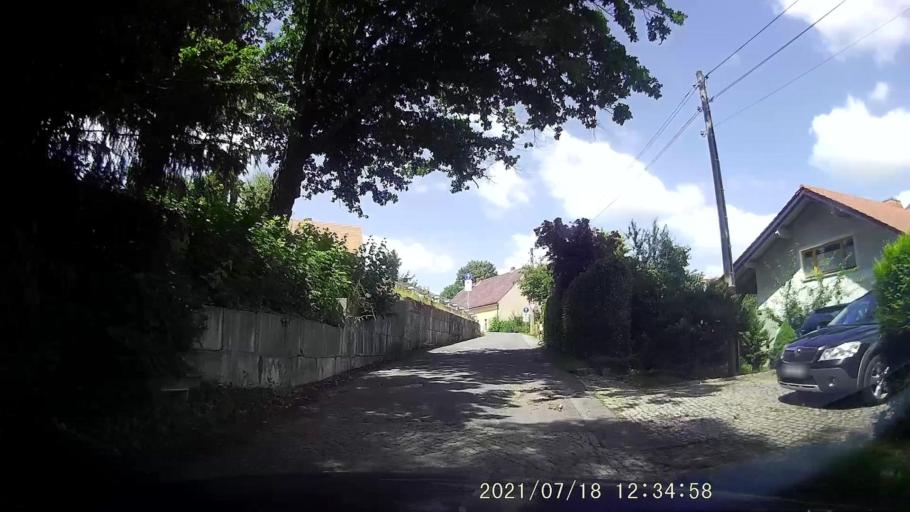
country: DE
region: Saxony
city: Konigshain
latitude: 51.1813
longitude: 14.8781
